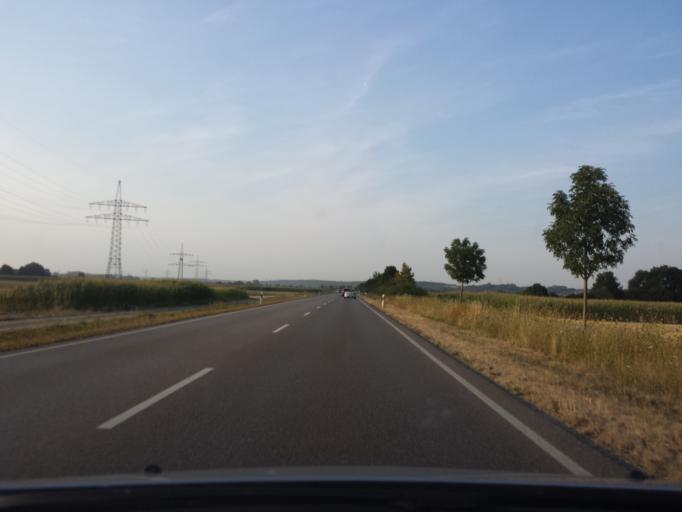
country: DE
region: Bavaria
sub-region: Swabia
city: Friedberg
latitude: 48.3725
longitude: 10.9606
